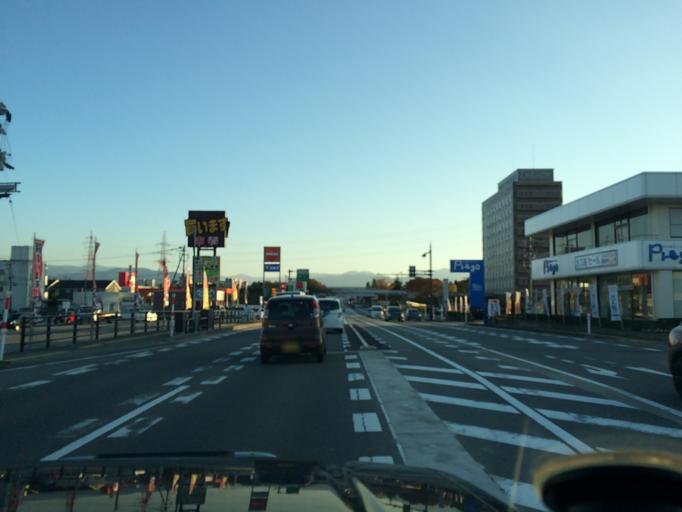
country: JP
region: Toyama
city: Toyama-shi
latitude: 36.6567
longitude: 137.2097
